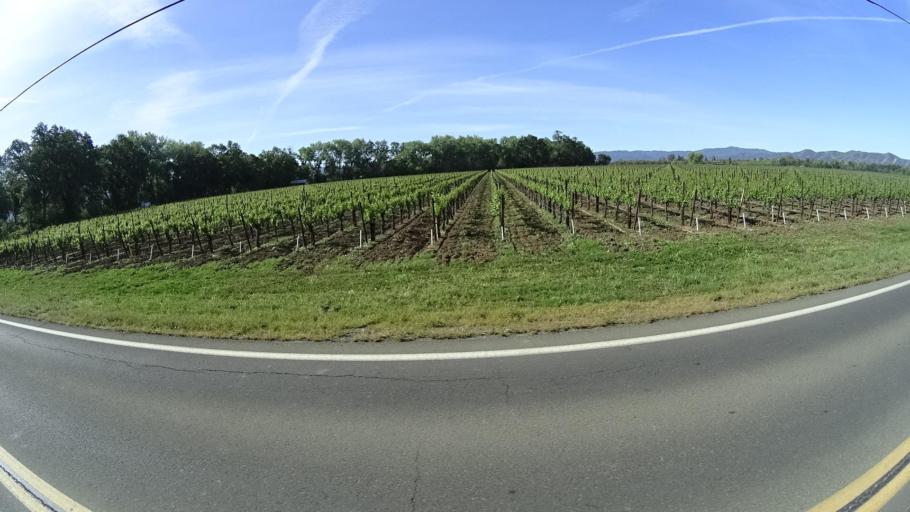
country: US
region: California
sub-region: Lake County
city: Kelseyville
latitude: 39.0150
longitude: -122.8629
